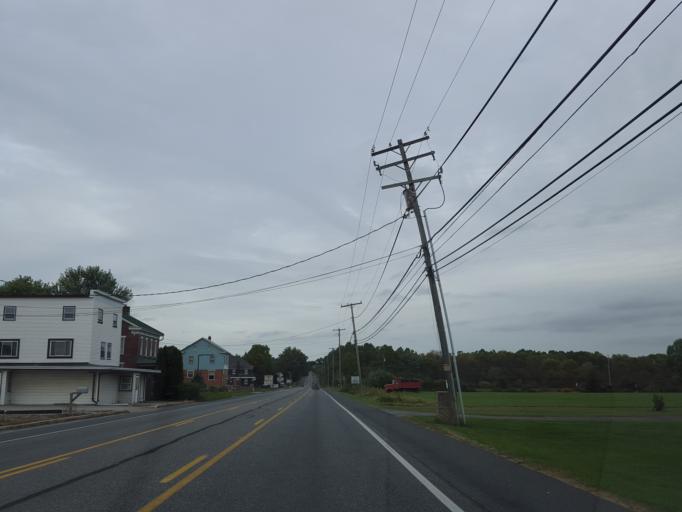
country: US
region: Pennsylvania
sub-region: York County
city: Spring Grove
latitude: 39.9213
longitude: -76.8951
